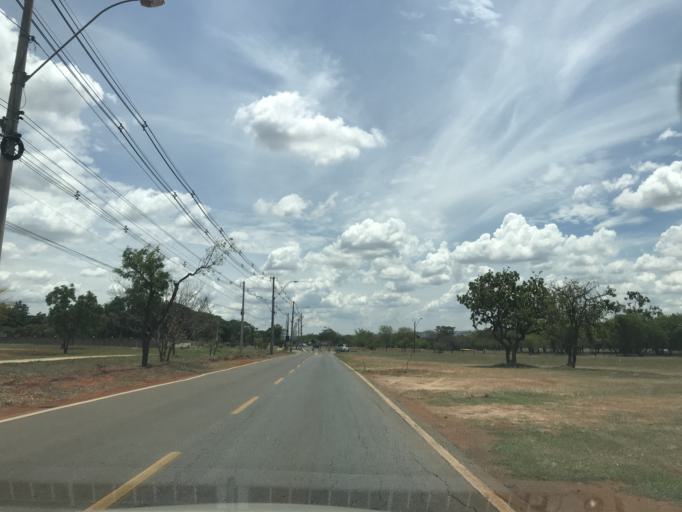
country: BR
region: Federal District
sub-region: Brasilia
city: Brasilia
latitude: -15.8664
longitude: -47.9391
